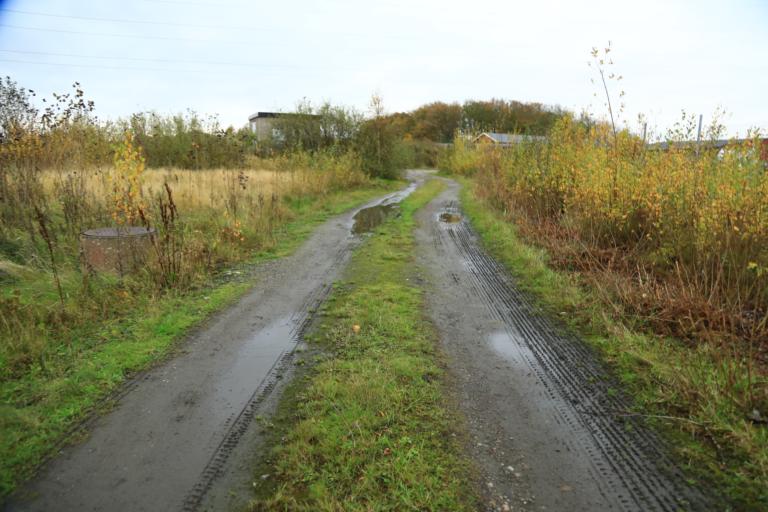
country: SE
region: Halland
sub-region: Varbergs Kommun
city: Varberg
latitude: 57.1267
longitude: 12.3021
